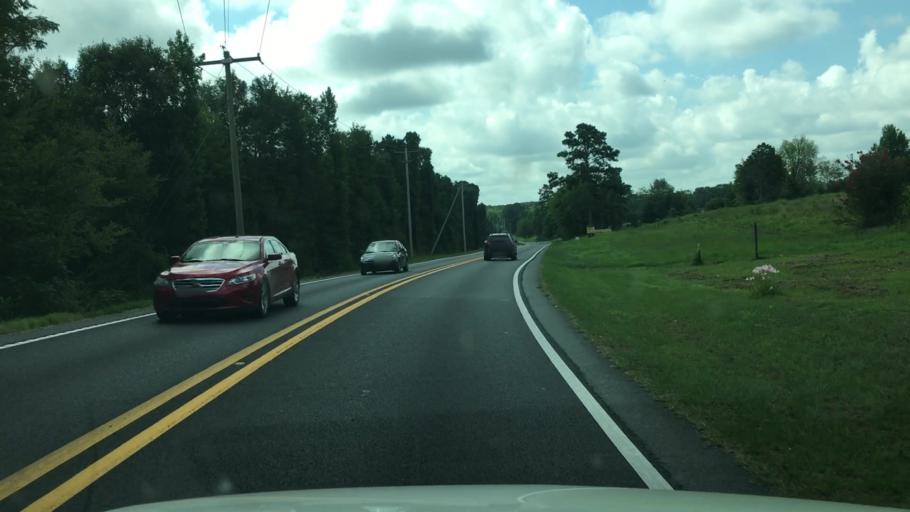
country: US
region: Arkansas
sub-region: Garland County
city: Lake Hamilton
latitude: 34.3010
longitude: -93.1648
